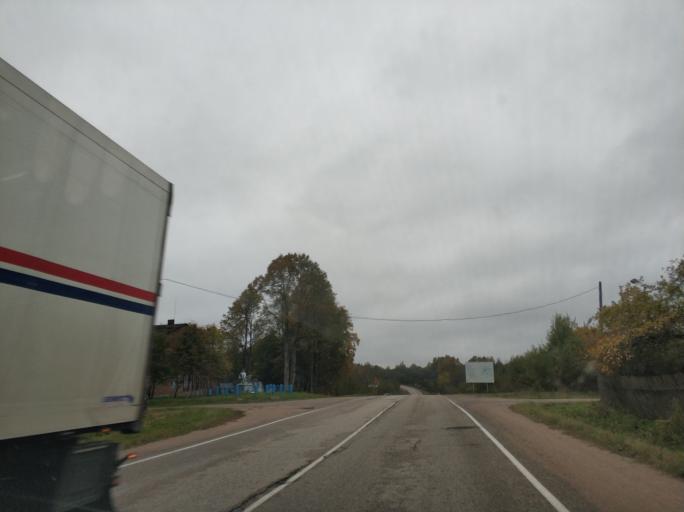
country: BY
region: Vitebsk
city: Rasony
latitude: 56.0569
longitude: 28.7136
